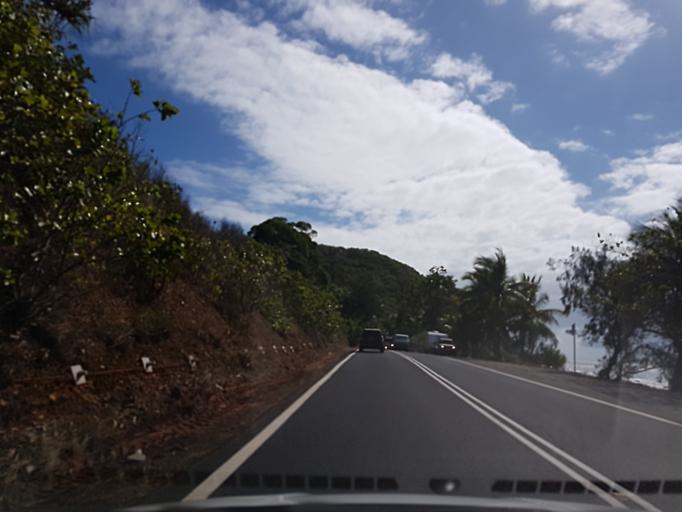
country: AU
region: Queensland
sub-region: Cairns
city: Port Douglas
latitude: -16.5799
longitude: 145.5121
